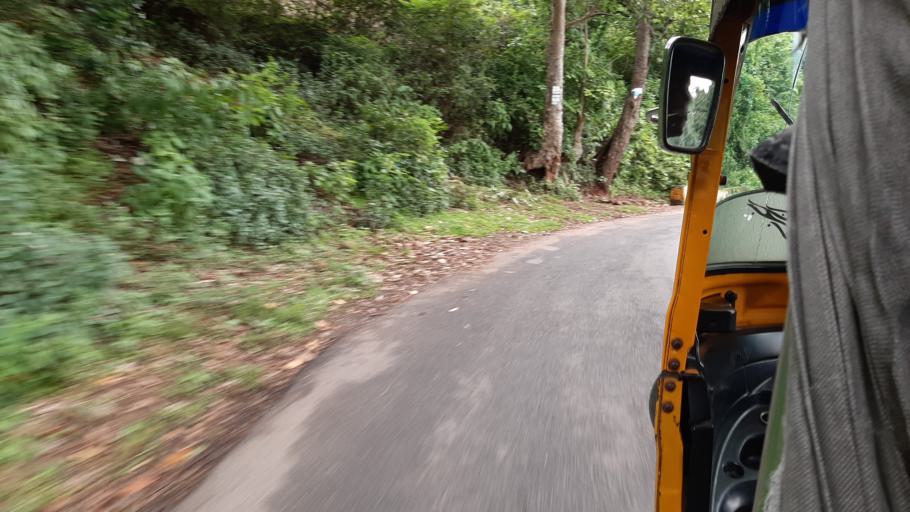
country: IN
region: Andhra Pradesh
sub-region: Vizianagaram District
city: Salur
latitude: 18.2434
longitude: 83.0255
